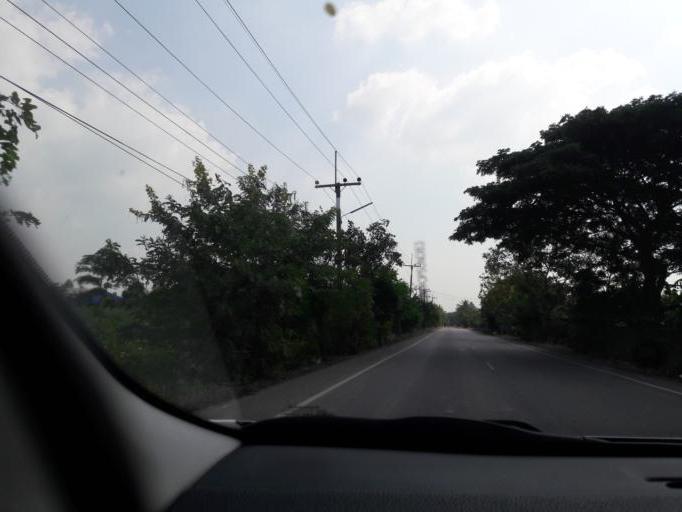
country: TH
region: Ang Thong
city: Ang Thong
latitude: 14.5770
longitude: 100.4280
